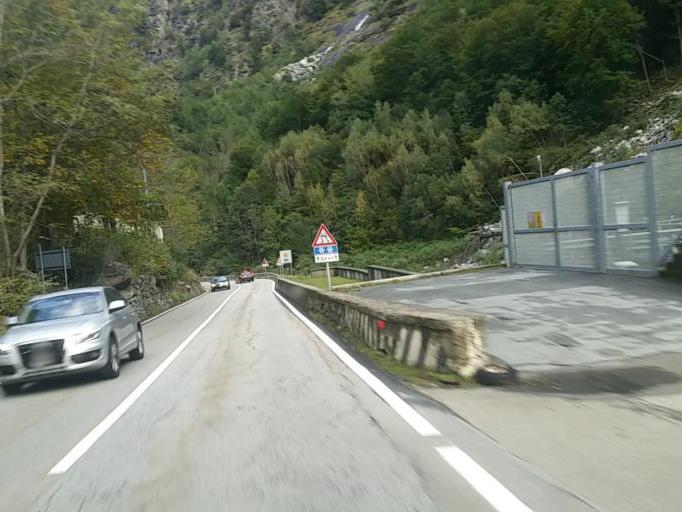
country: IT
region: Piedmont
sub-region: Provincia Verbano-Cusio-Ossola
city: Trasquera
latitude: 46.1962
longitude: 8.1526
